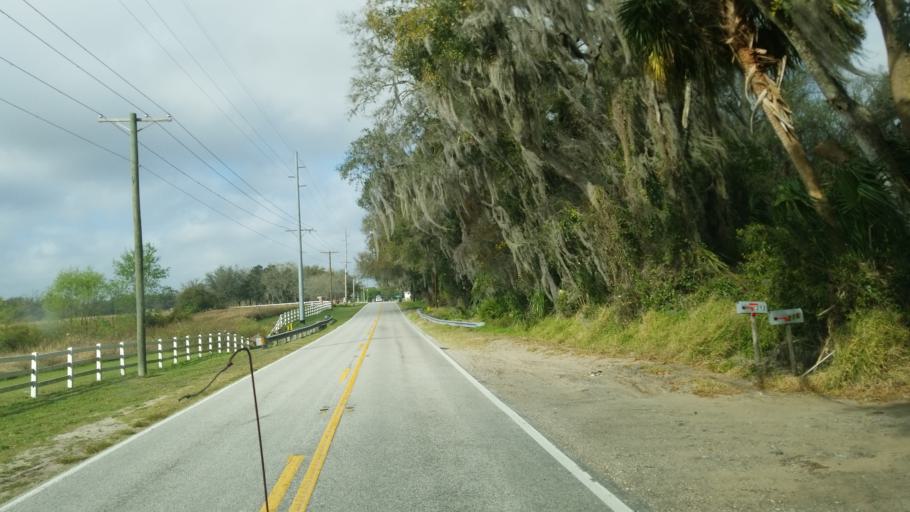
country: US
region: Florida
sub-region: Hillsborough County
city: Fish Hawk
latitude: 27.8866
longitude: -82.1224
